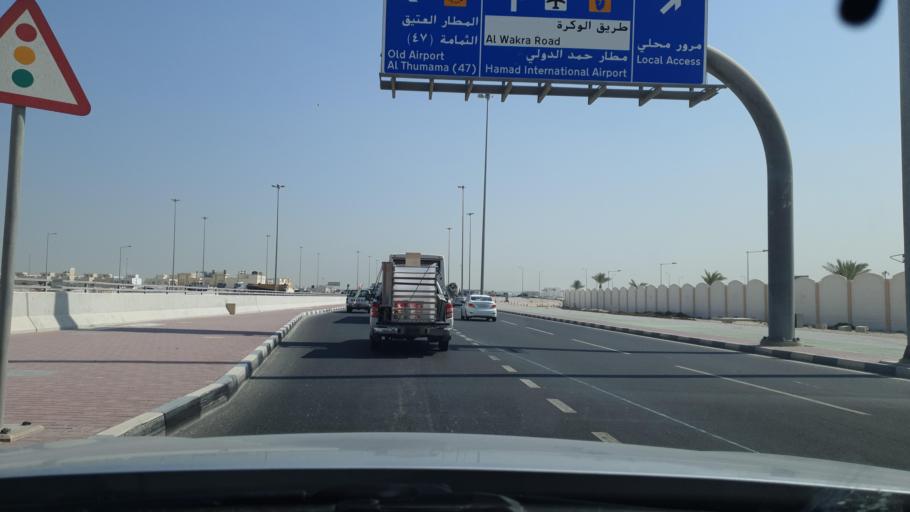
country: QA
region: Baladiyat ad Dawhah
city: Doha
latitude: 25.2259
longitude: 51.5548
